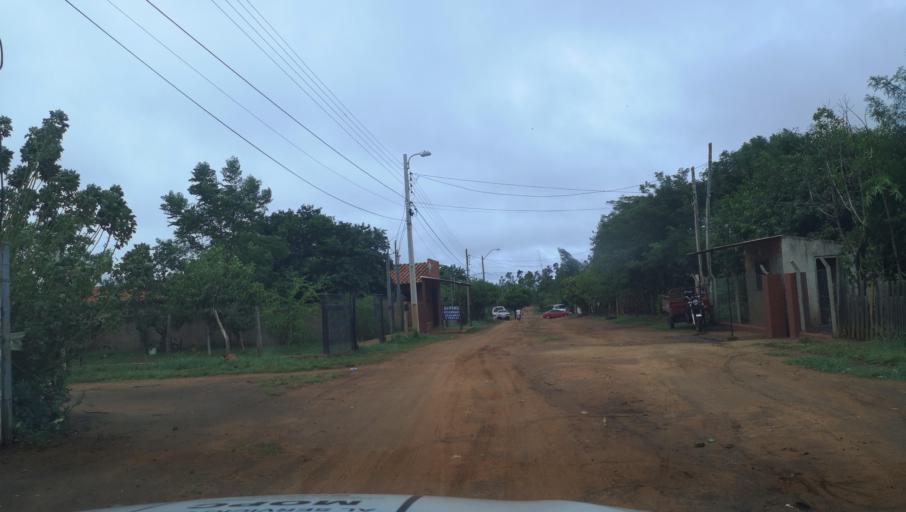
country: PY
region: Misiones
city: Santa Maria
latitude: -26.8993
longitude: -57.0367
